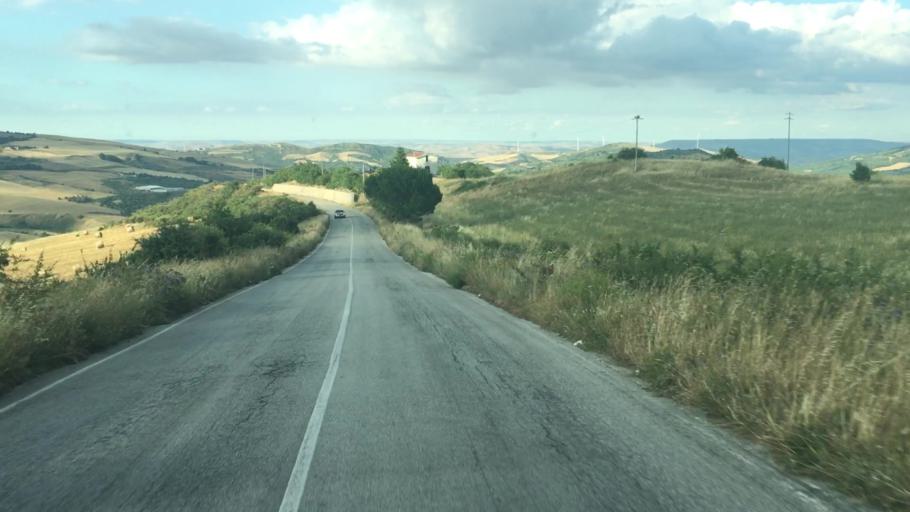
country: IT
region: Basilicate
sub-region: Provincia di Potenza
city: Tolve
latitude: 40.6946
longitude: 15.9908
